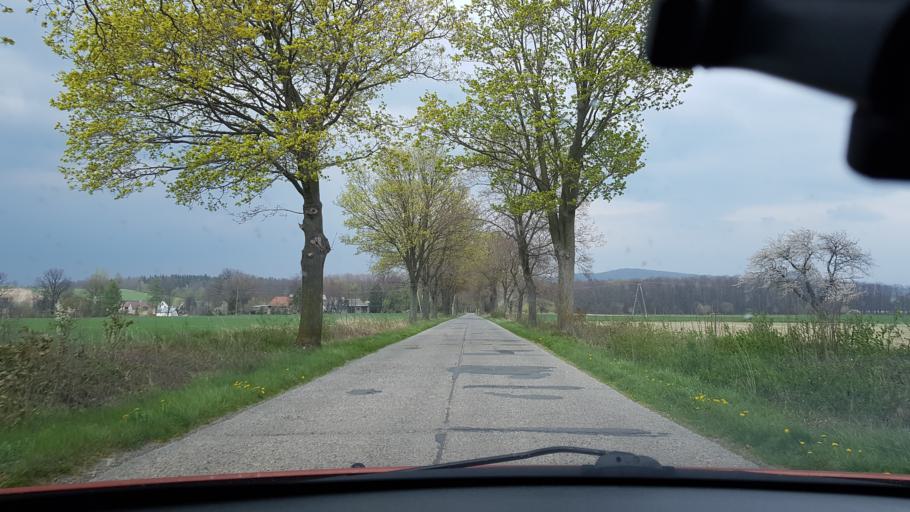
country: PL
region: Lower Silesian Voivodeship
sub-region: Powiat klodzki
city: Bystrzyca Klodzka
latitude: 50.3478
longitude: 16.5981
